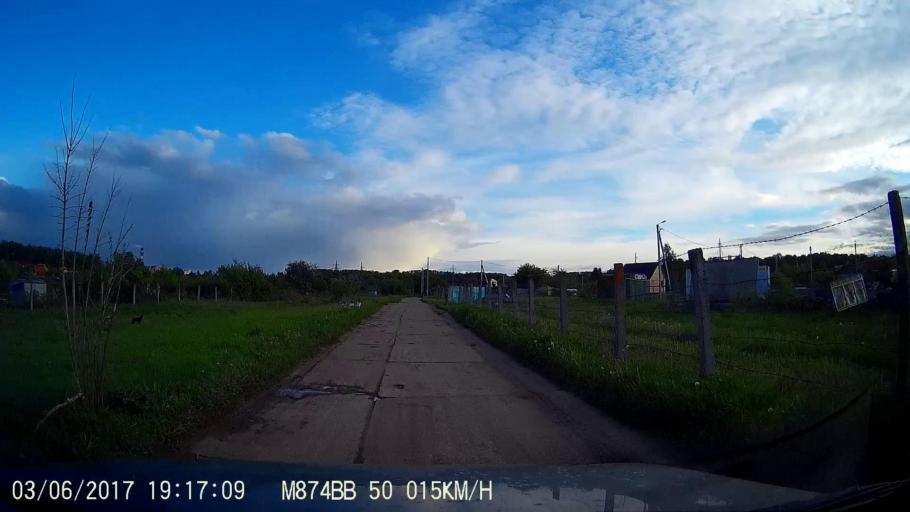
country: RU
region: Moskovskaya
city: Sychevo
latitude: 55.0704
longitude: 38.7375
